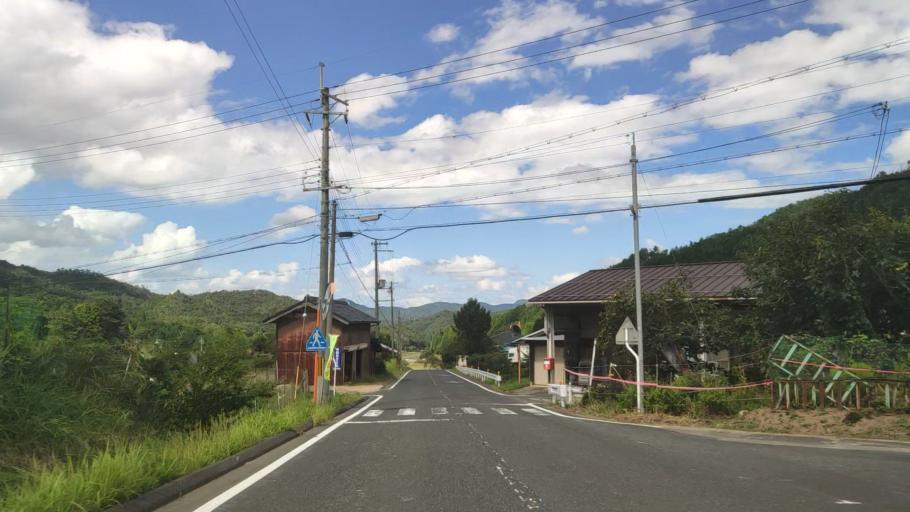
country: JP
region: Hyogo
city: Toyooka
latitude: 35.5455
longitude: 134.9782
